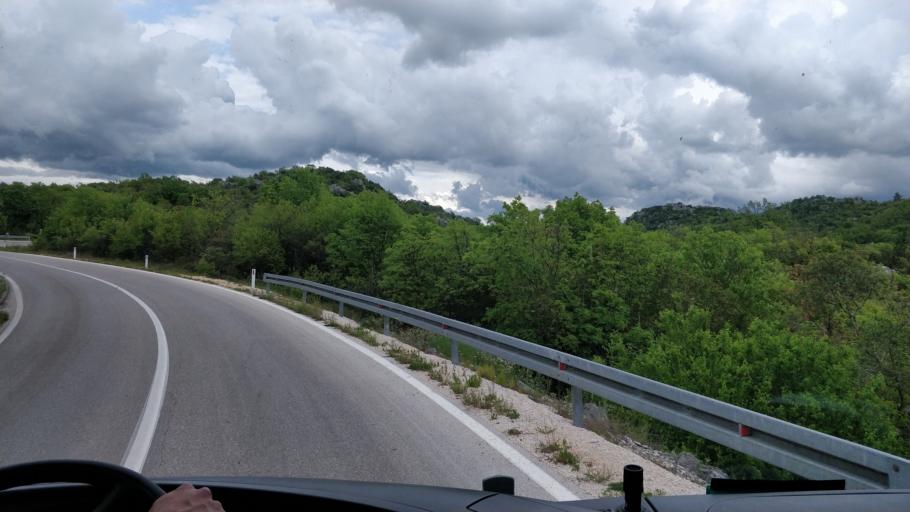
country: BA
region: Federation of Bosnia and Herzegovina
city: Ljubuski
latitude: 43.1741
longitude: 17.4869
